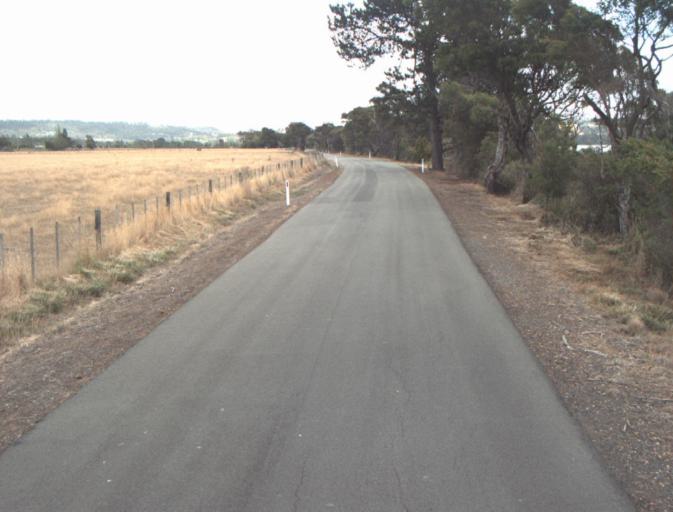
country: AU
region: Tasmania
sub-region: Launceston
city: Mayfield
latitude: -41.2829
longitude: 147.0085
